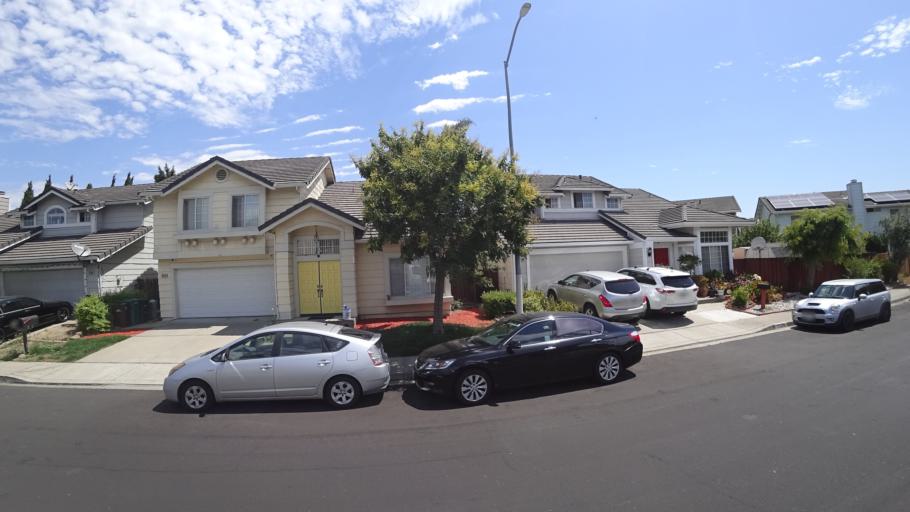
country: US
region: California
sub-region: Alameda County
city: Hayward
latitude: 37.6473
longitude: -122.0774
